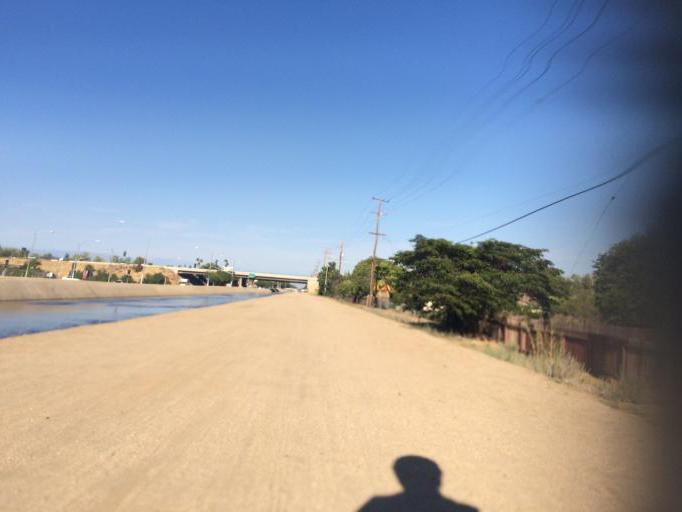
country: US
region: California
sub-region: Fresno County
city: Fresno
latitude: 36.7648
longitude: -119.7528
